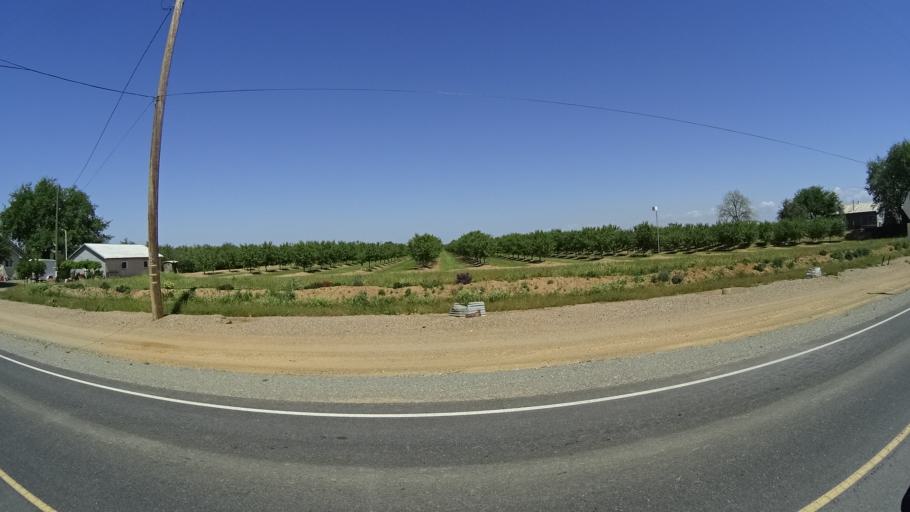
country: US
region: California
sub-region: Glenn County
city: Hamilton City
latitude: 39.7665
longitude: -122.0928
